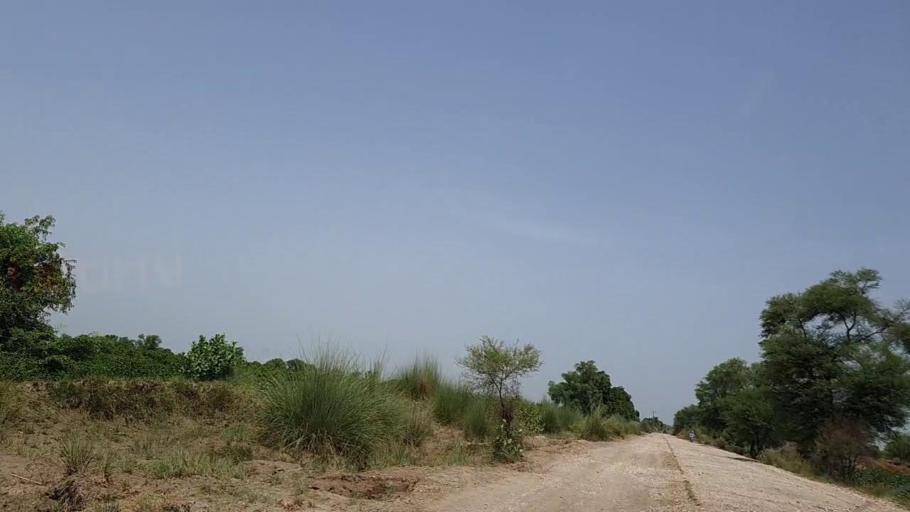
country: PK
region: Sindh
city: Tharu Shah
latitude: 26.9170
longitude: 68.0012
